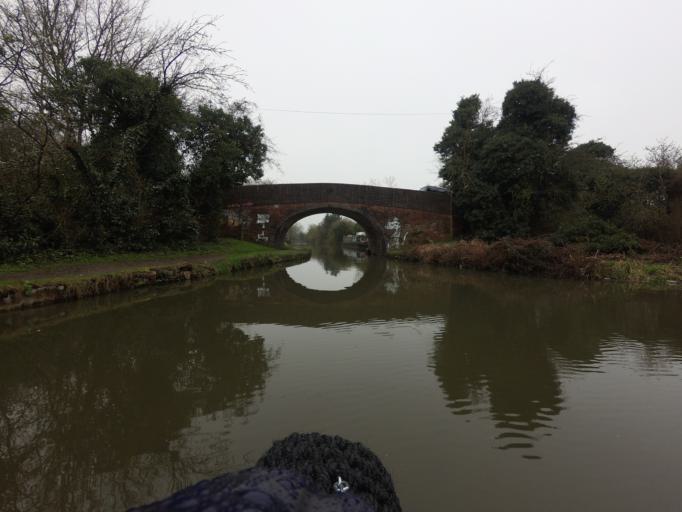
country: GB
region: England
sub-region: Milton Keynes
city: Simpson
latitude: 52.0097
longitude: -0.7163
